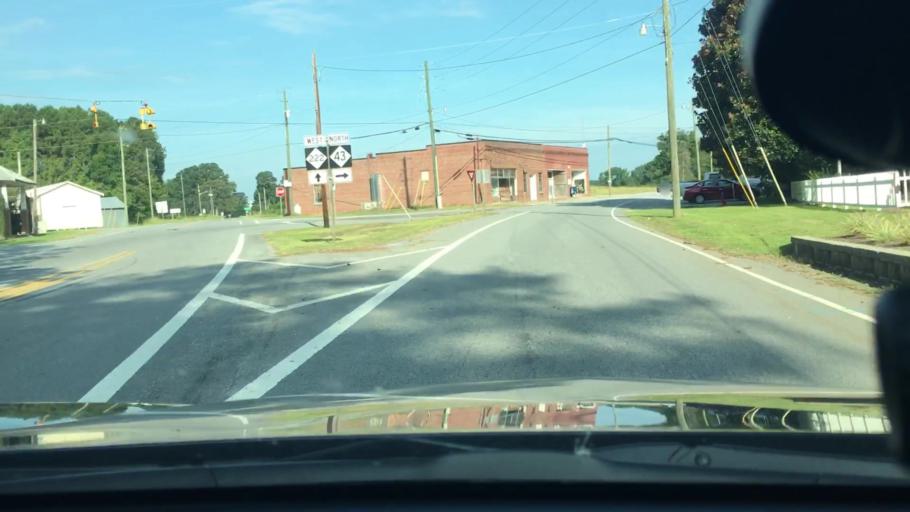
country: US
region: North Carolina
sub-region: Pitt County
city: Farmville
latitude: 35.6983
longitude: -77.5131
